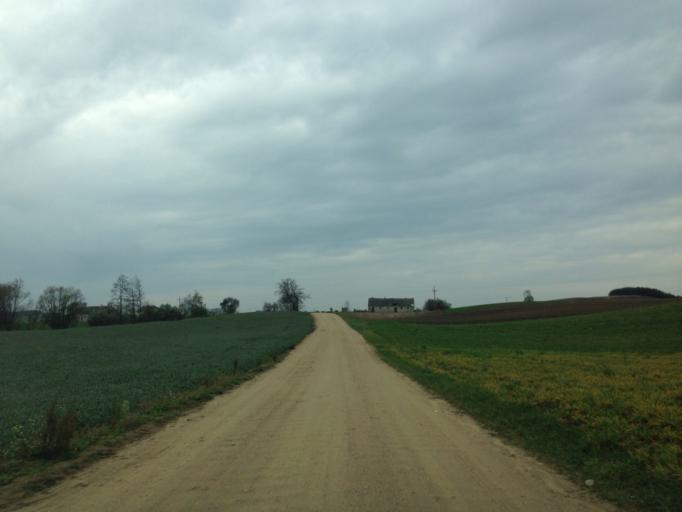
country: PL
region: Kujawsko-Pomorskie
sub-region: Powiat brodnicki
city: Bartniczka
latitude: 53.2716
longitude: 19.6579
